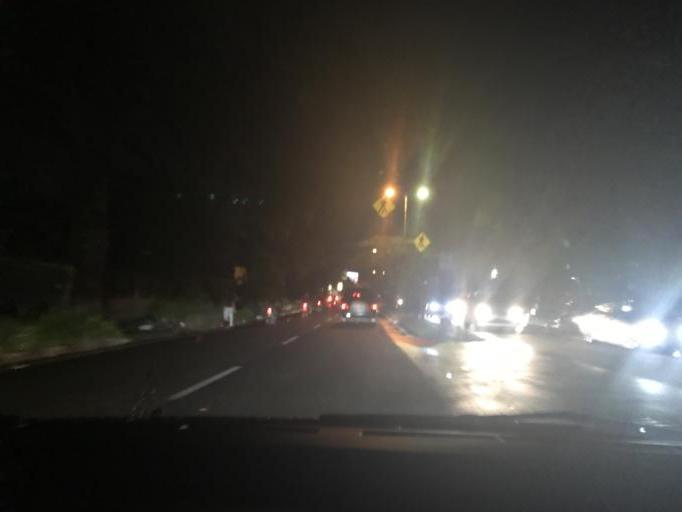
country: ID
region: West Java
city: Bandung
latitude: -6.9114
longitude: 107.6331
